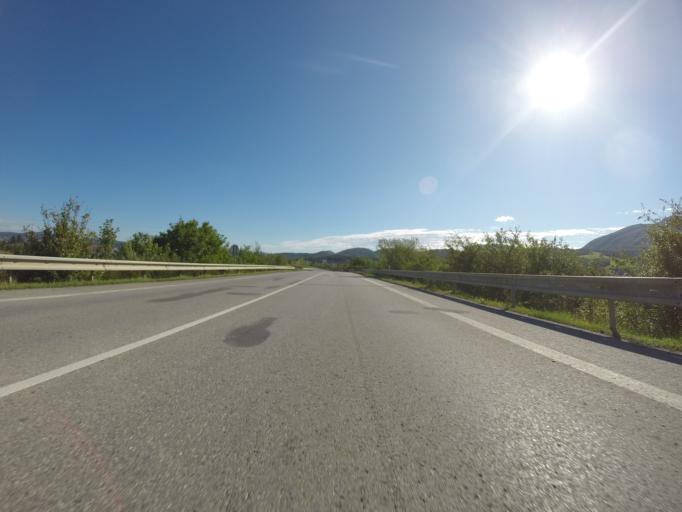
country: SK
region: Nitriansky
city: Puchov
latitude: 49.0464
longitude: 18.3053
